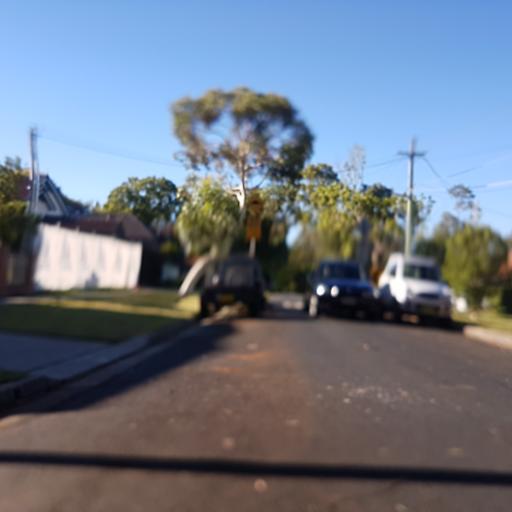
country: AU
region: New South Wales
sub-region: Willoughby
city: Castle Cove
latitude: -33.8004
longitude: 151.2040
